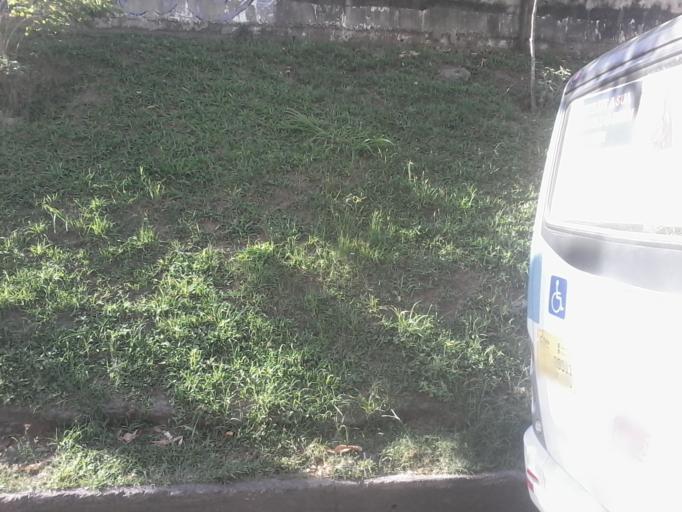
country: BR
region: Rio de Janeiro
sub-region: Rio De Janeiro
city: Rio de Janeiro
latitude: -22.9935
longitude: -43.2540
